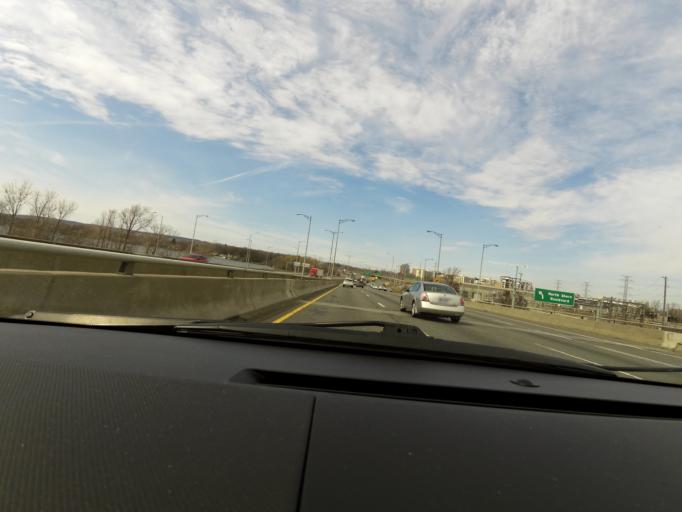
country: CA
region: Ontario
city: Hamilton
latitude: 43.3082
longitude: -79.8027
